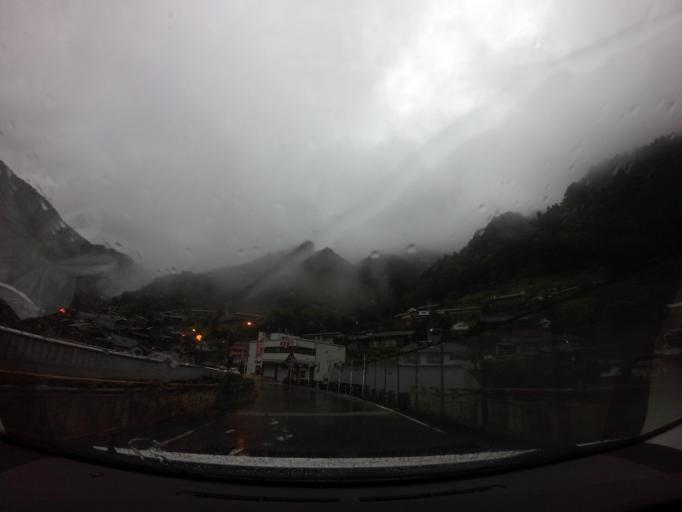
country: JP
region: Wakayama
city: Shingu
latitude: 33.9483
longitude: 135.8043
